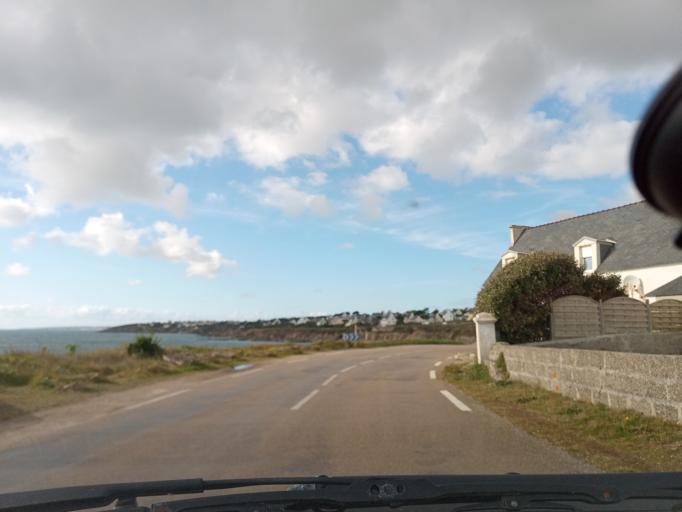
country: FR
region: Brittany
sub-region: Departement du Finistere
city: Plozevet
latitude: 47.9785
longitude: -4.4485
